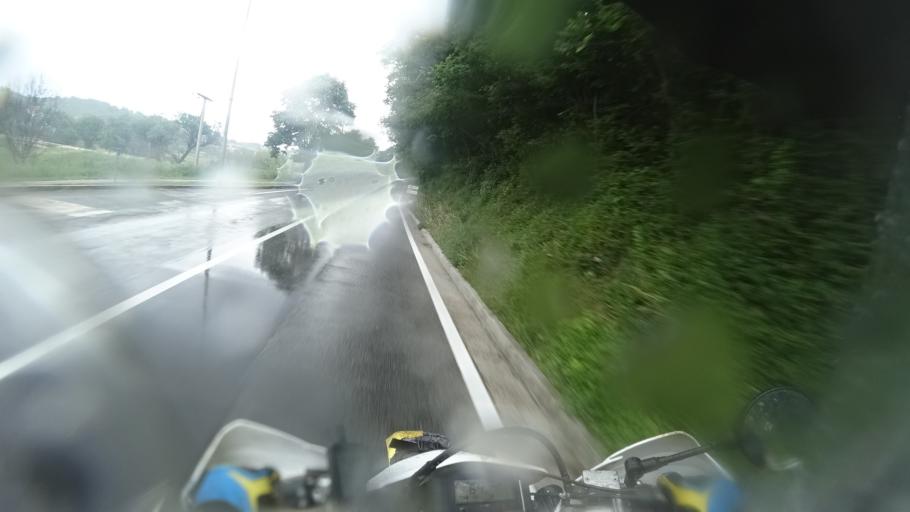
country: HR
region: Sibensko-Kniniska
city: Knin
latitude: 44.0407
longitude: 16.2081
